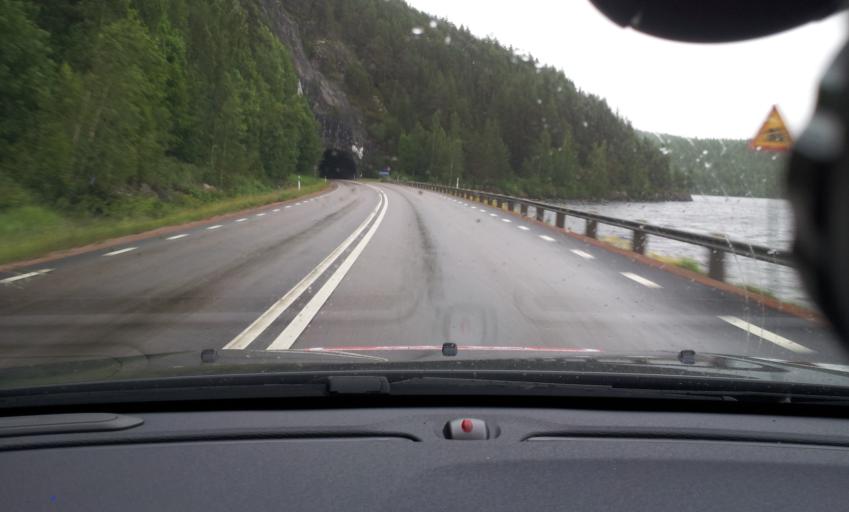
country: SE
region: Jaemtland
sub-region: Ragunda Kommun
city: Hammarstrand
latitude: 63.1389
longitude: 16.0256
